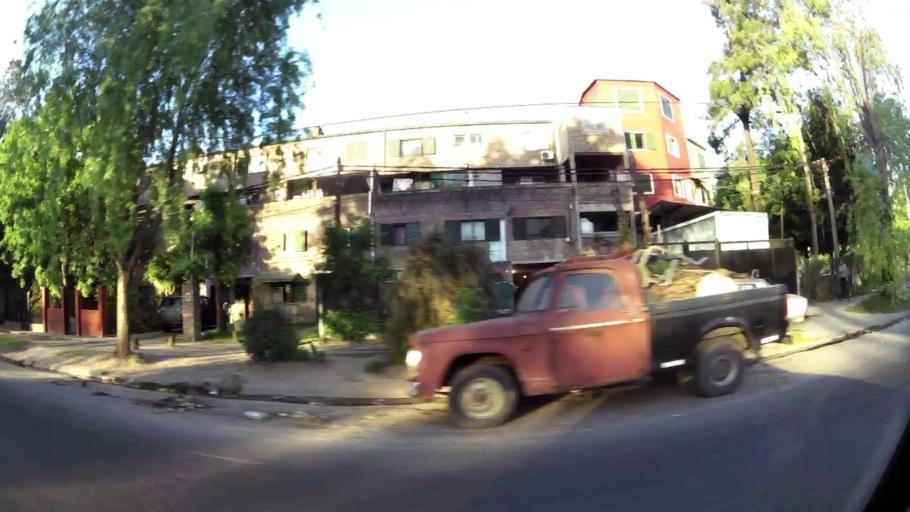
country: AR
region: Buenos Aires
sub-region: Partido de San Isidro
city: San Isidro
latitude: -34.4712
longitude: -58.5391
